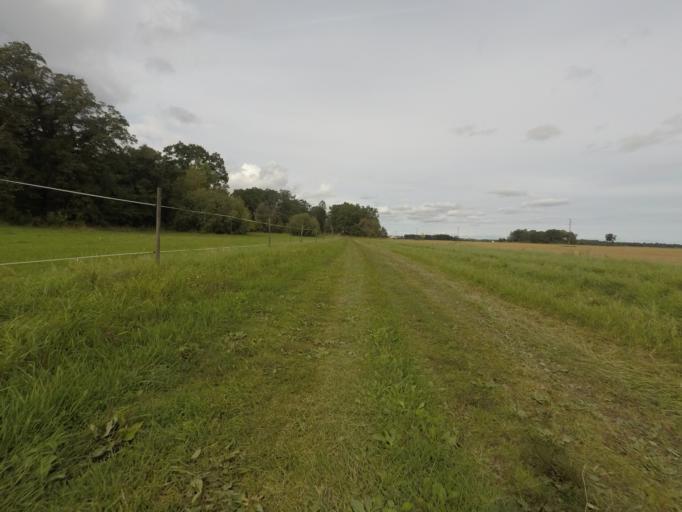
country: SE
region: Vaestmanland
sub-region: Kungsors Kommun
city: Kungsoer
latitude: 59.4538
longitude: 16.0510
